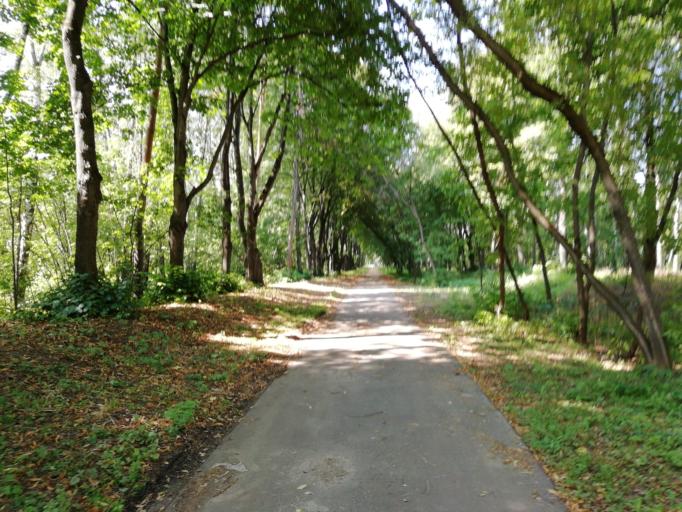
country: RU
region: Moscow
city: Davydkovo
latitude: 55.7282
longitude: 37.4684
